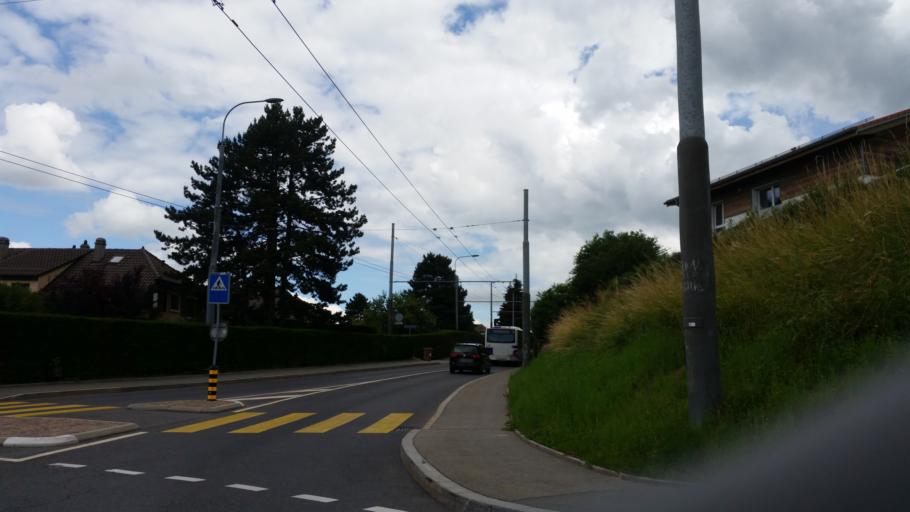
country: CH
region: Vaud
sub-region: Lausanne District
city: Le Mont-sur-Lausanne
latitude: 46.5513
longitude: 6.6326
